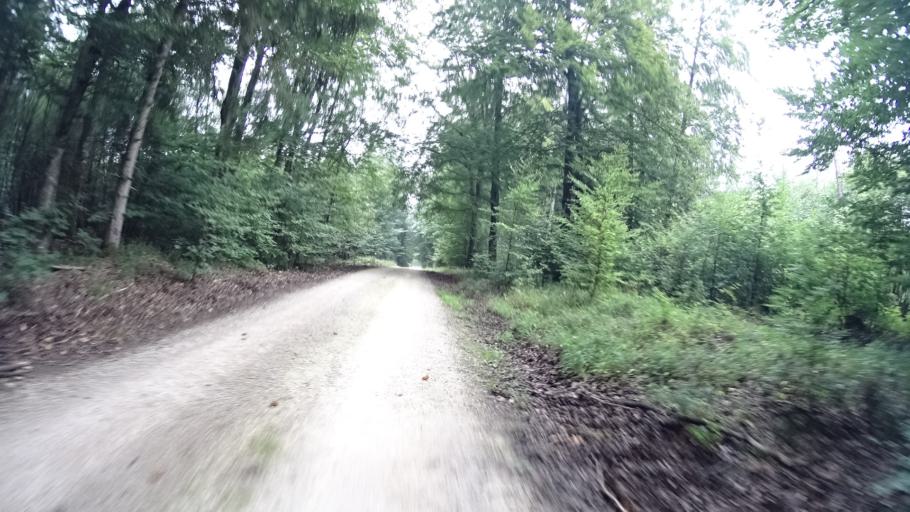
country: DE
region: Bavaria
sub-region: Upper Bavaria
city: Stammham
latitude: 48.8838
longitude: 11.5102
